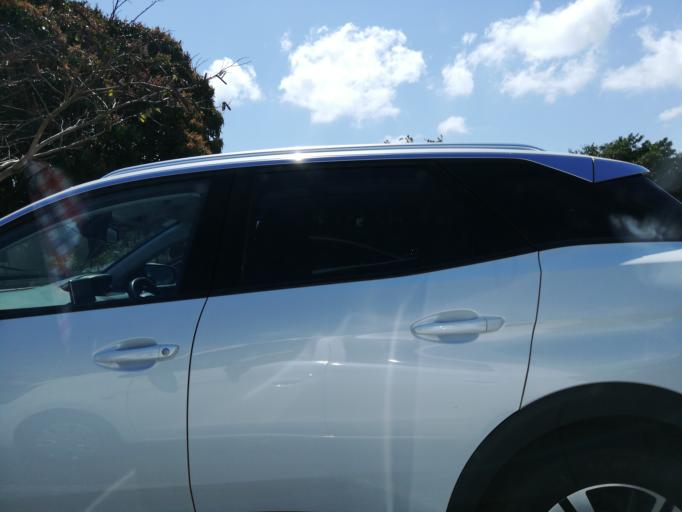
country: MU
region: Moka
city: Saint Pierre
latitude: -20.2250
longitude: 57.5254
